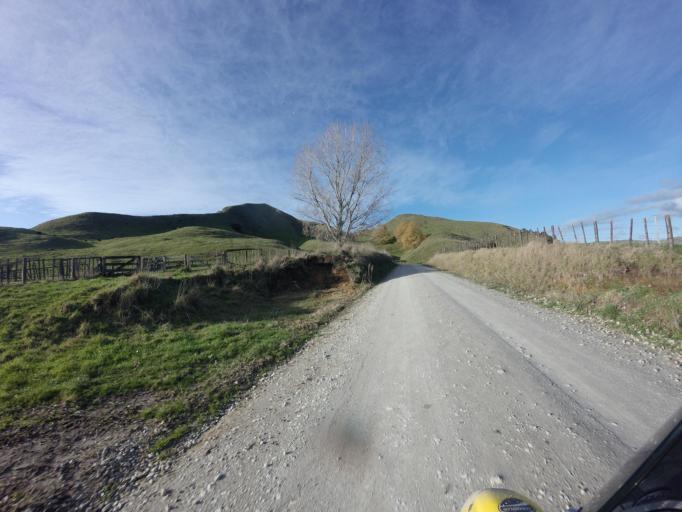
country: NZ
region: Hawke's Bay
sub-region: Wairoa District
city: Wairoa
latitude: -38.7202
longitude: 177.5730
